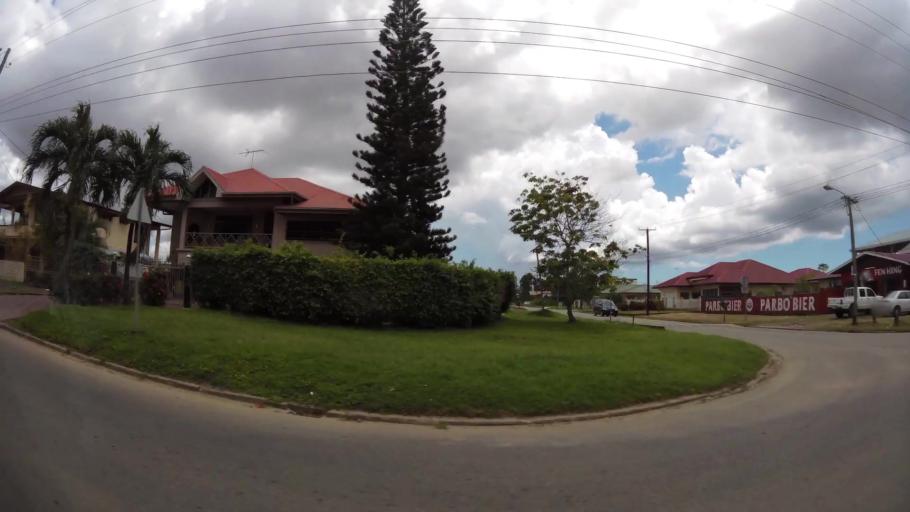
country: SR
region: Paramaribo
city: Paramaribo
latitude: 5.8585
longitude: -55.1344
